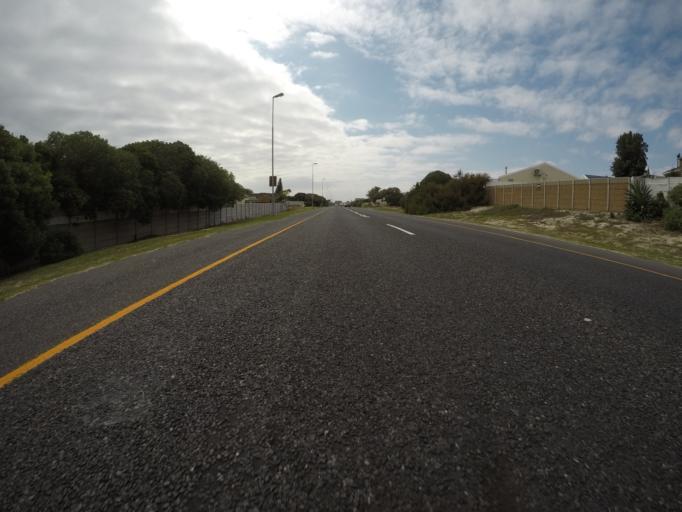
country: ZA
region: Western Cape
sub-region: City of Cape Town
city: Sunset Beach
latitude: -33.7204
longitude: 18.4466
